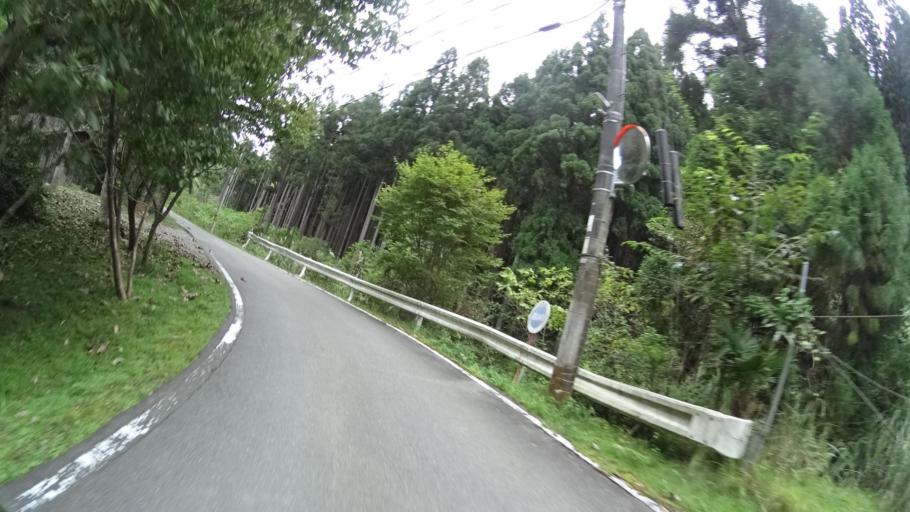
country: JP
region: Shiga Prefecture
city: Kitahama
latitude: 35.2334
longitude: 135.7859
